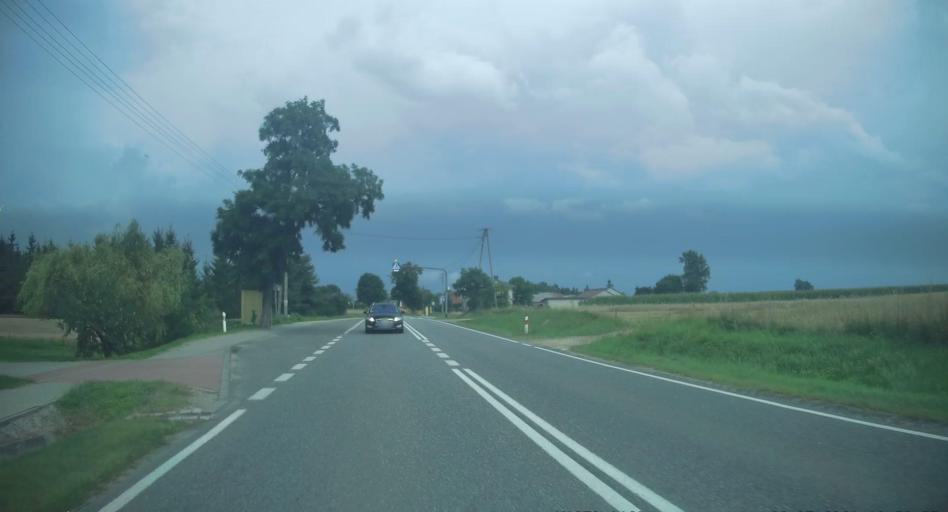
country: PL
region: Lodz Voivodeship
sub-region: Powiat skierniewicki
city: Gluchow
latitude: 51.7713
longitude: 20.1503
